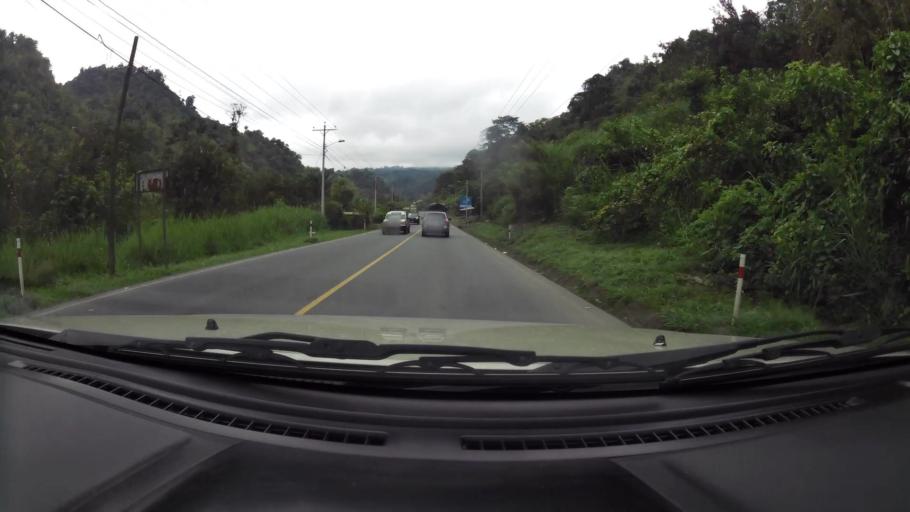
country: EC
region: Santo Domingo de los Tsachilas
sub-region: Canton Santo Domingo de los Colorados
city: Santo Domingo de los Colorados
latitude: -0.3165
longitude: -79.0134
